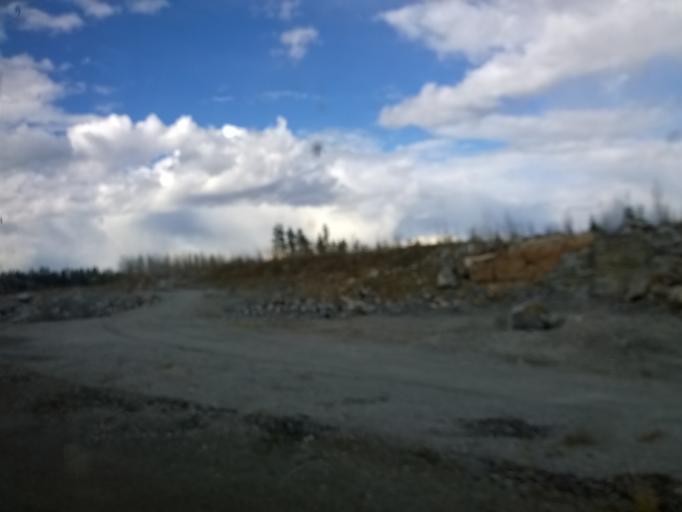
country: FI
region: Pirkanmaa
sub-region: Tampere
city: Tampere
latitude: 61.4578
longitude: 23.7918
